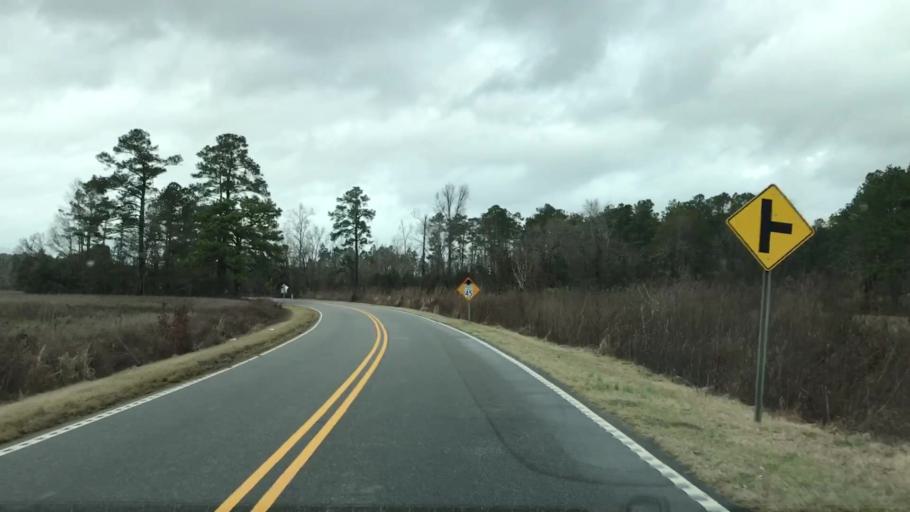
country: US
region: South Carolina
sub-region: Florence County
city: Johnsonville
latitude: 33.6599
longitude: -79.3043
